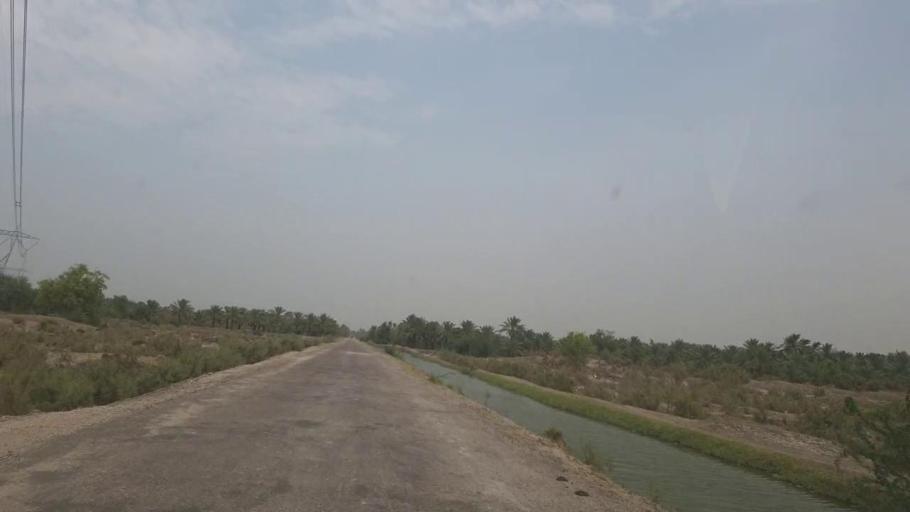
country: PK
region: Sindh
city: Kot Diji
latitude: 27.4274
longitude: 68.6912
